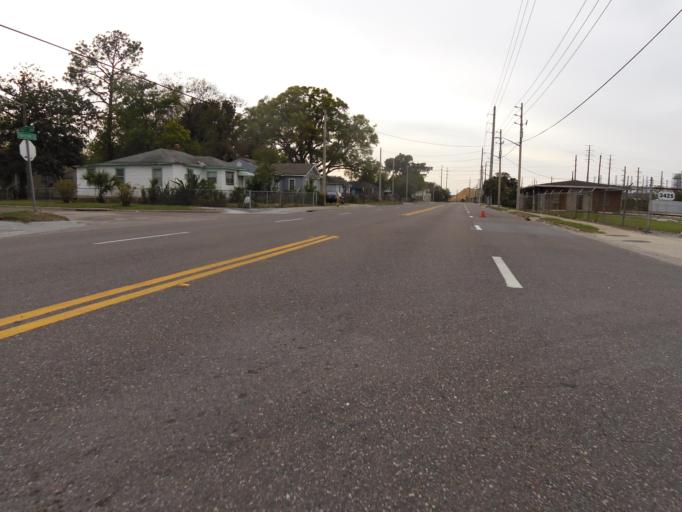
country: US
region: Florida
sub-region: Duval County
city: Jacksonville
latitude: 30.3603
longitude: -81.6270
